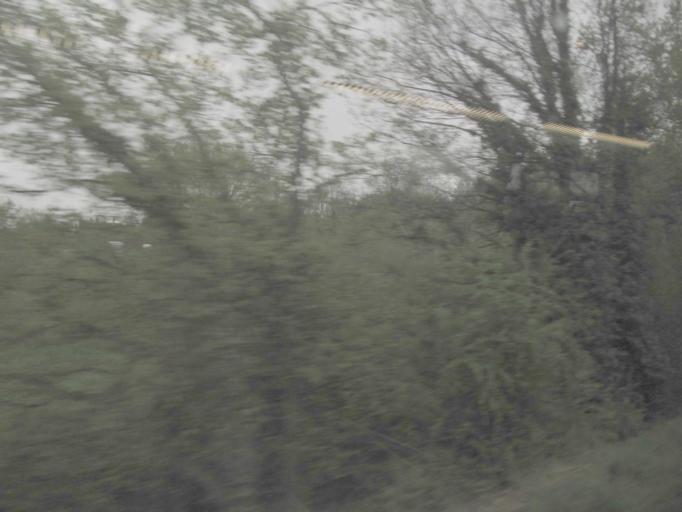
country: GB
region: England
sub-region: Wokingham
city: Wokingham
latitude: 51.3987
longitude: -0.8366
